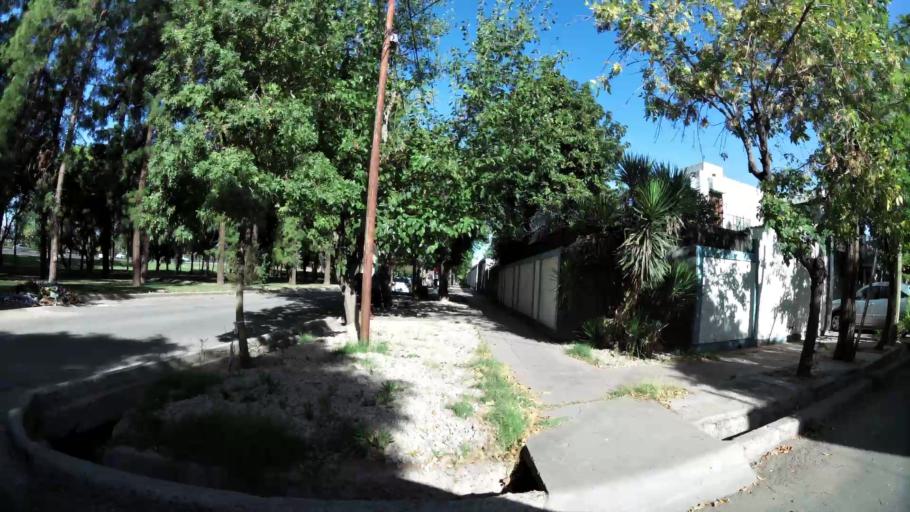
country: AR
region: Mendoza
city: Mendoza
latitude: -32.8997
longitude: -68.8075
